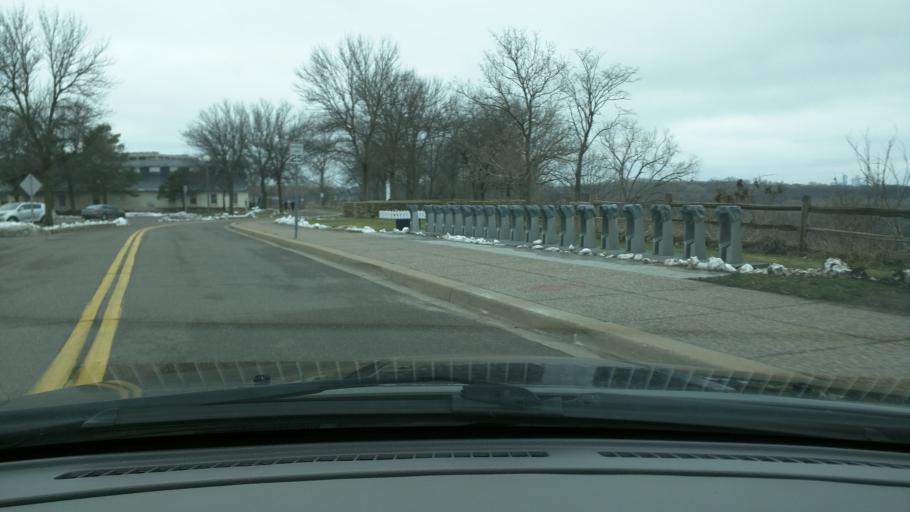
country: US
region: Minnesota
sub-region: Dakota County
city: Mendota Heights
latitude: 44.8938
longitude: -93.1872
